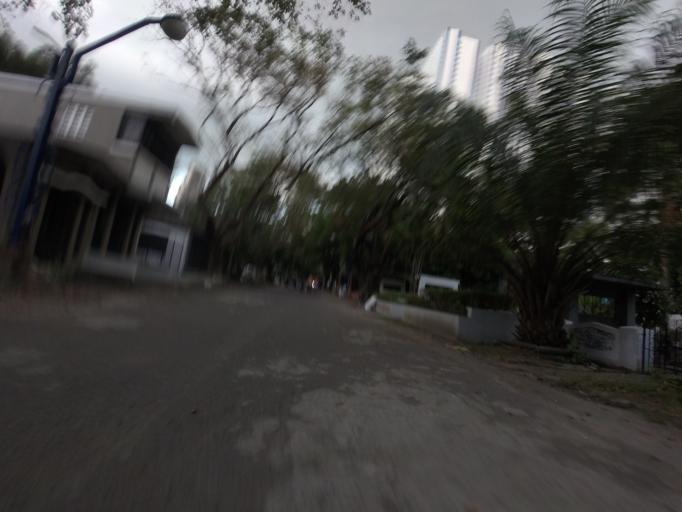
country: PH
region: Metro Manila
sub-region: Makati City
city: Makati City
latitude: 14.5652
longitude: 121.0206
